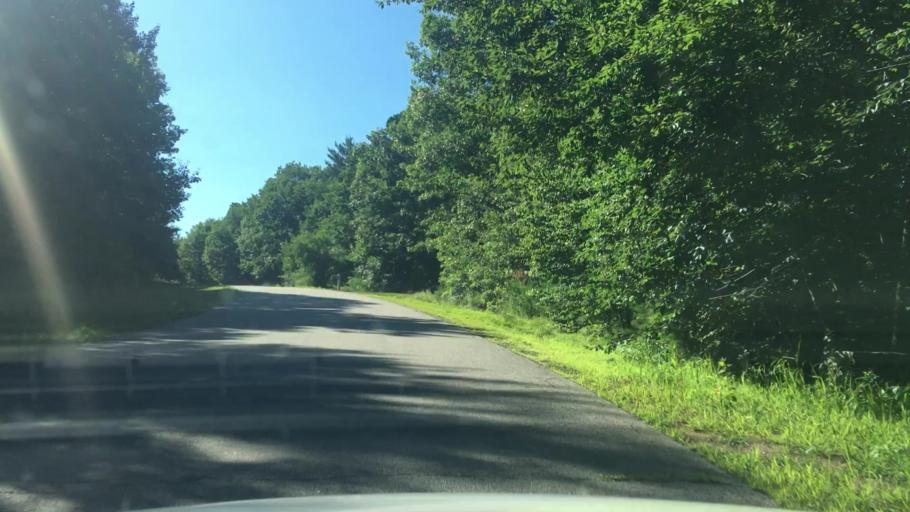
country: US
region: New Hampshire
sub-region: Rockingham County
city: Newmarket
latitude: 43.0358
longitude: -70.9594
